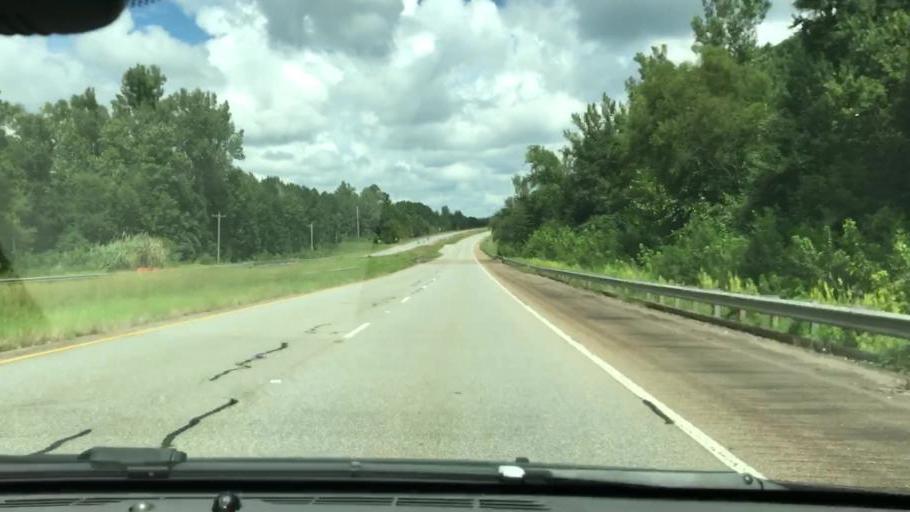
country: US
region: Georgia
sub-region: Stewart County
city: Lumpkin
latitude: 32.1020
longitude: -84.8114
